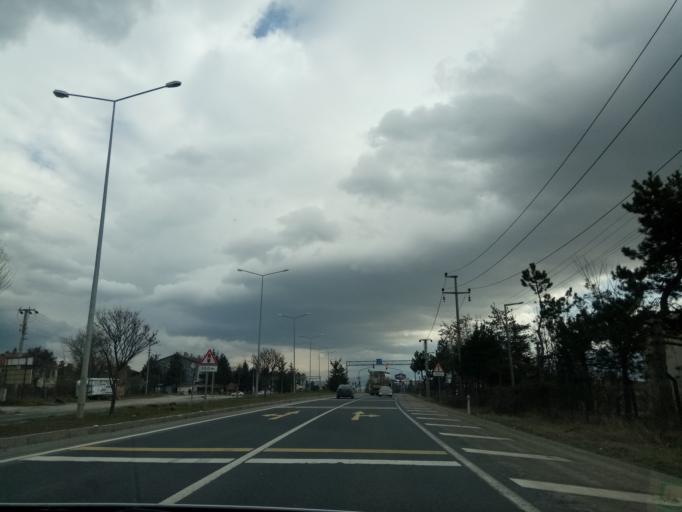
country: TR
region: Bolu
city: Bolu
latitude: 40.7021
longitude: 31.5091
